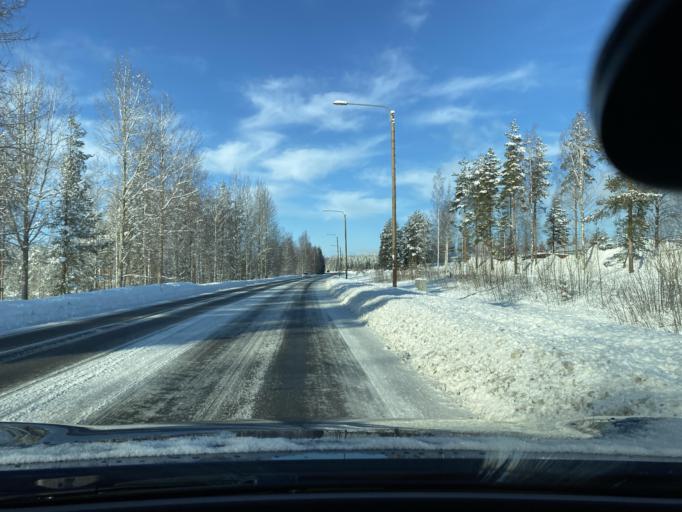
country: FI
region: Southern Savonia
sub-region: Mikkeli
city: Kangasniemi
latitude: 62.0066
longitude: 26.6441
